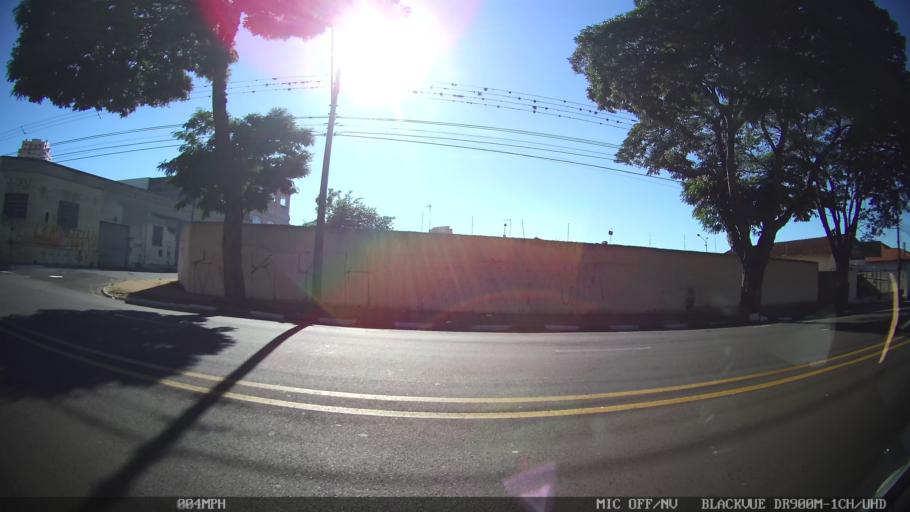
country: BR
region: Sao Paulo
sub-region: Franca
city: Franca
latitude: -20.5401
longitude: -47.4146
